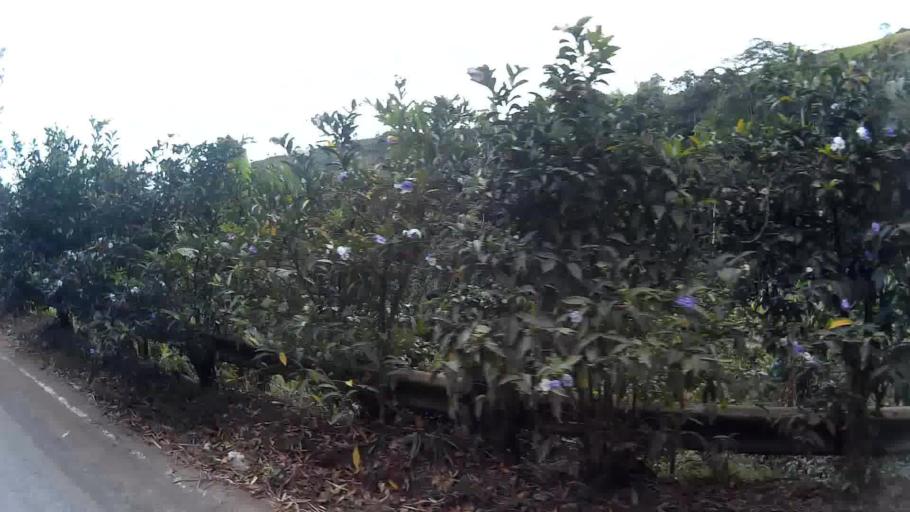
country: CO
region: Risaralda
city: Marsella
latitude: 4.9122
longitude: -75.7364
